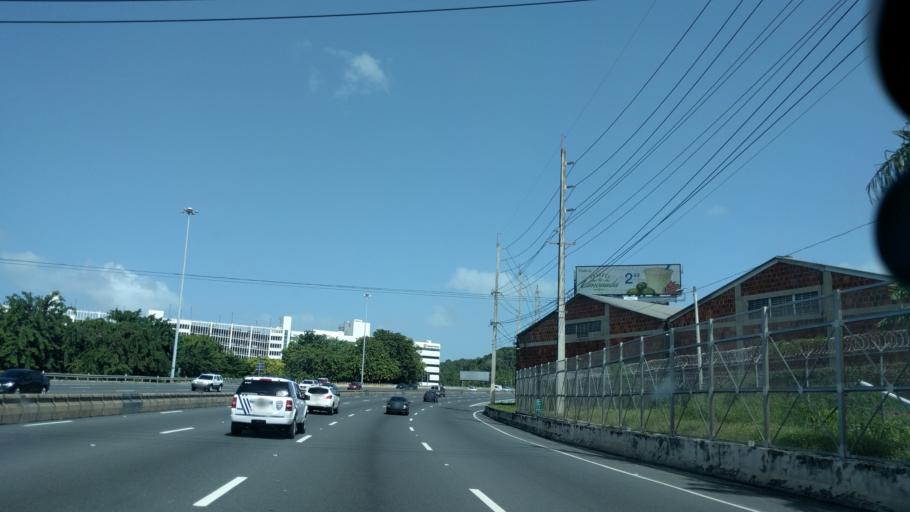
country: PR
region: Catano
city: Catano
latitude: 18.4220
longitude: -66.1126
